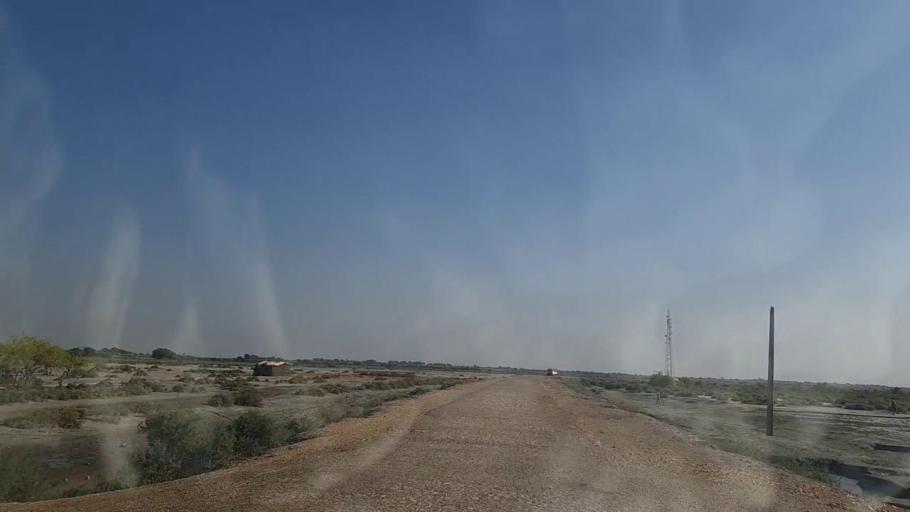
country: PK
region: Sindh
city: Mirpur Batoro
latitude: 24.5958
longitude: 68.1704
